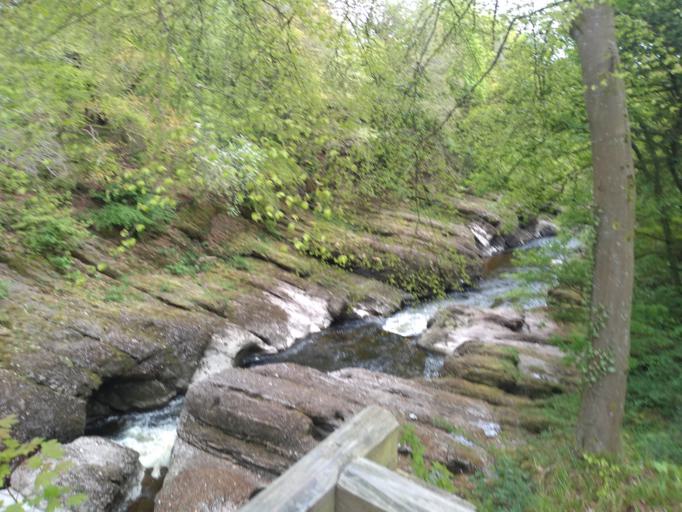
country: GB
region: Scotland
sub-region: Perth and Kinross
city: Blairgowrie
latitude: 56.5990
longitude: -3.3407
